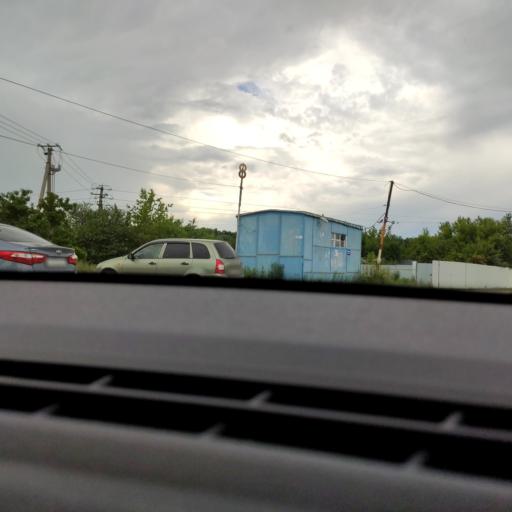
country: RU
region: Samara
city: Podstepki
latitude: 53.5131
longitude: 49.0705
